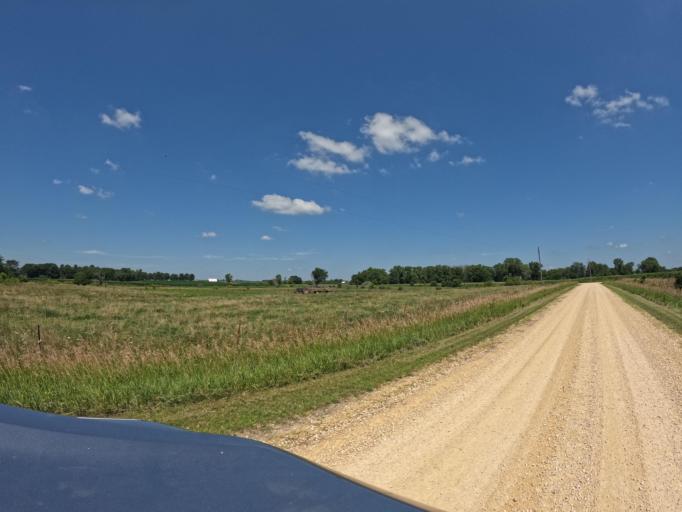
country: US
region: Iowa
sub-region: Clinton County
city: De Witt
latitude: 41.7787
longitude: -90.4288
